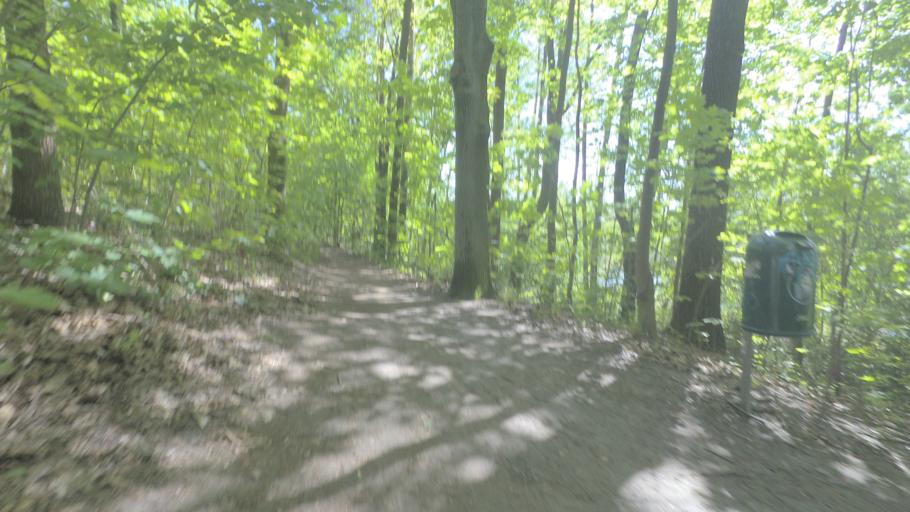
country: DE
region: Brandenburg
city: Erkner
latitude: 52.4281
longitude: 13.7640
